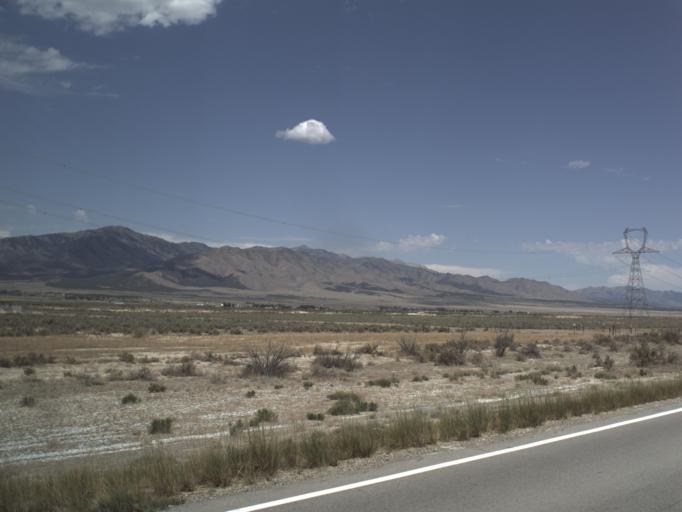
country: US
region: Utah
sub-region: Tooele County
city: Tooele
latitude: 40.3097
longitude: -112.4043
